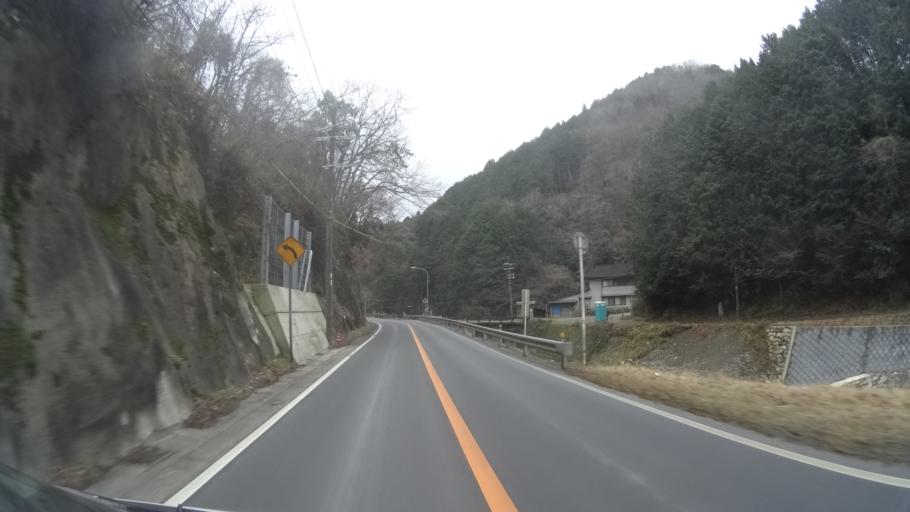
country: JP
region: Kyoto
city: Fukuchiyama
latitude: 35.3474
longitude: 135.0631
